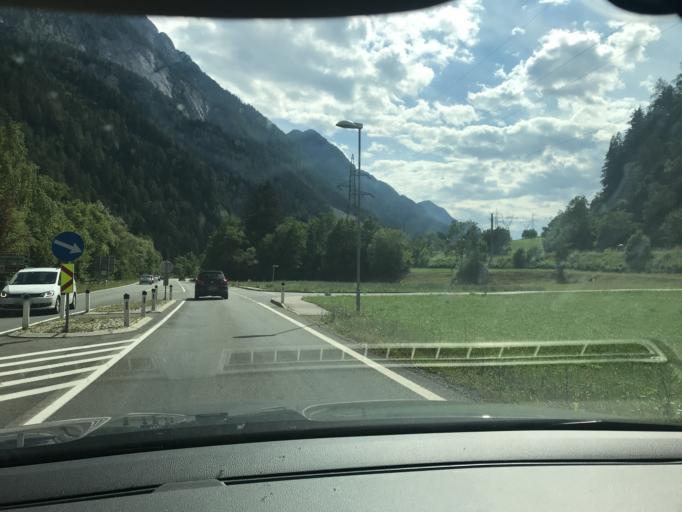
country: AT
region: Tyrol
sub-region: Politischer Bezirk Lienz
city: Leisach
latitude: 46.7976
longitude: 12.7355
